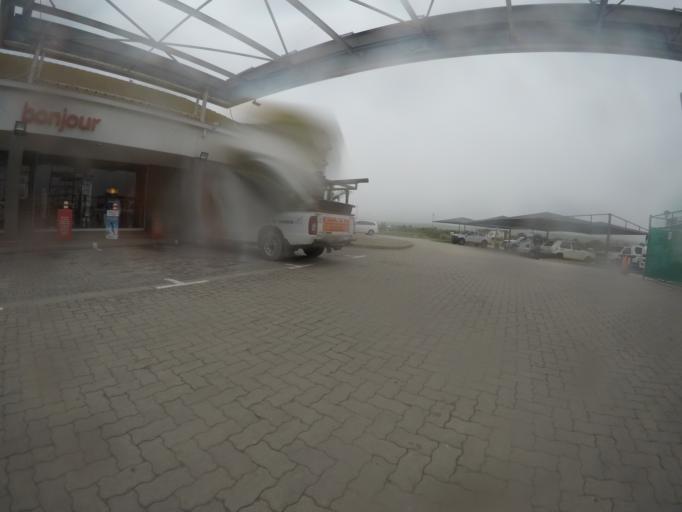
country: ZA
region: Western Cape
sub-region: Eden District Municipality
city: Mossel Bay
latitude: -34.1802
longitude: 22.0288
